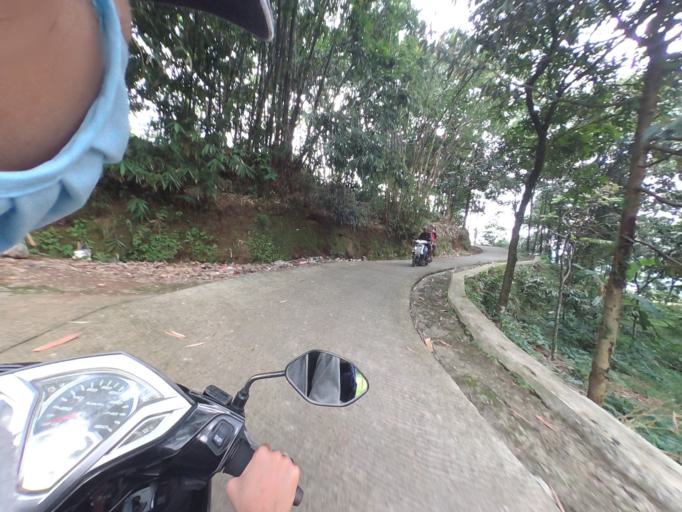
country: ID
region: West Java
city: Ciampea
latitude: -6.6868
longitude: 106.6535
